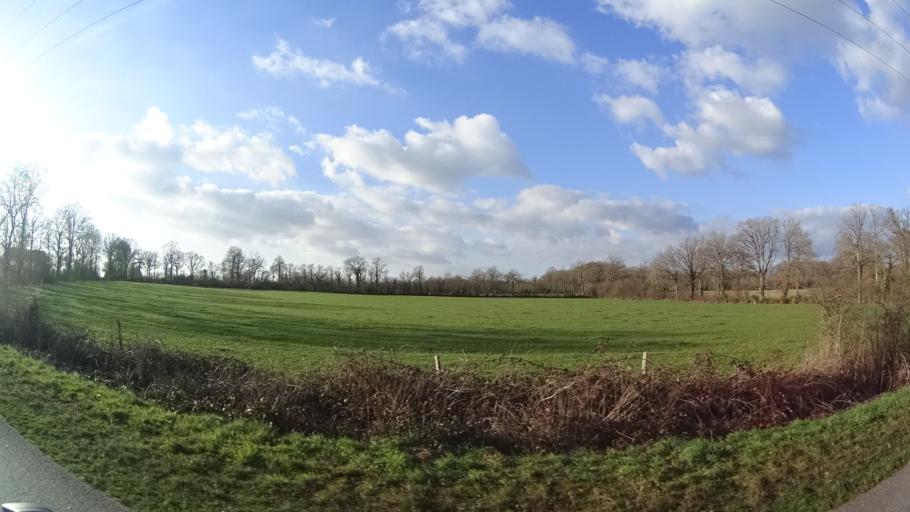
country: FR
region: Pays de la Loire
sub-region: Departement de la Loire-Atlantique
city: Plesse
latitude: 47.5713
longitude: -1.8667
